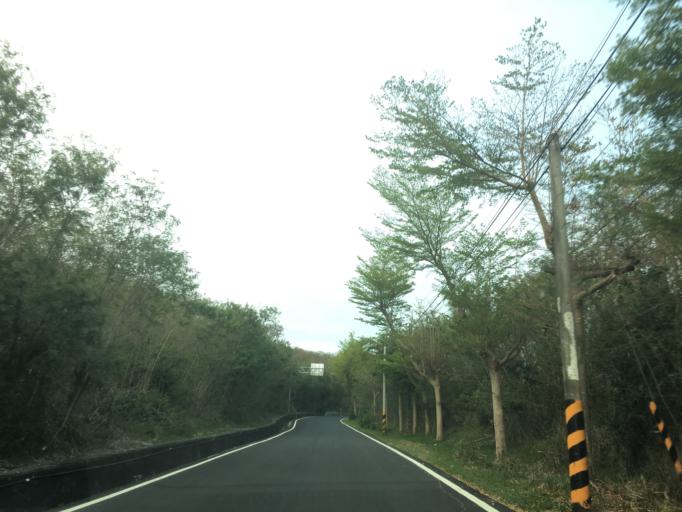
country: TW
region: Taiwan
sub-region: Taitung
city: Taitung
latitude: 22.7872
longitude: 121.1586
